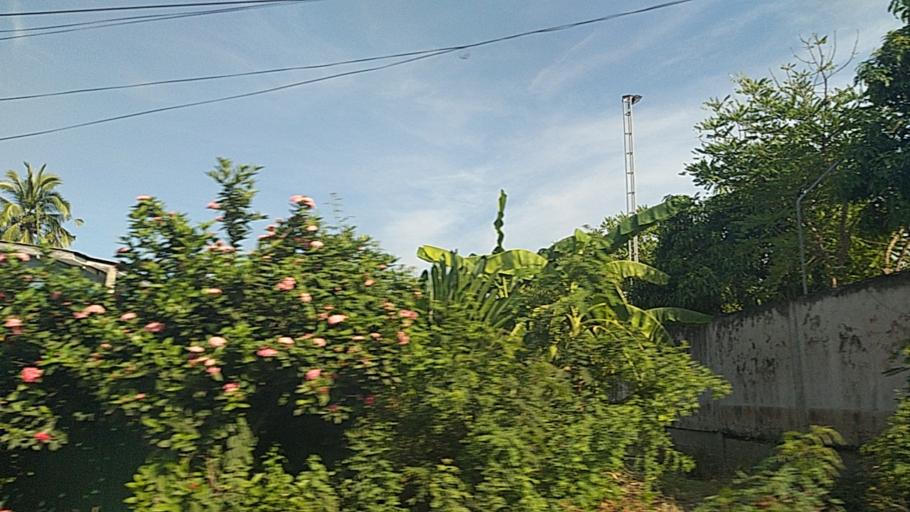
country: TH
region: Pathum Thani
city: Thanyaburi
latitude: 13.9986
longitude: 100.7306
